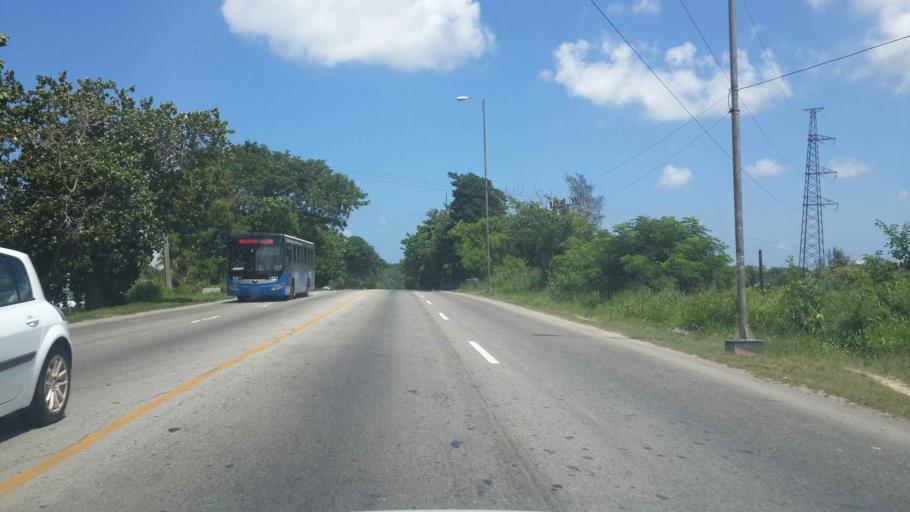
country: CU
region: La Habana
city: Guanabacoa
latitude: 23.1386
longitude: -82.3058
